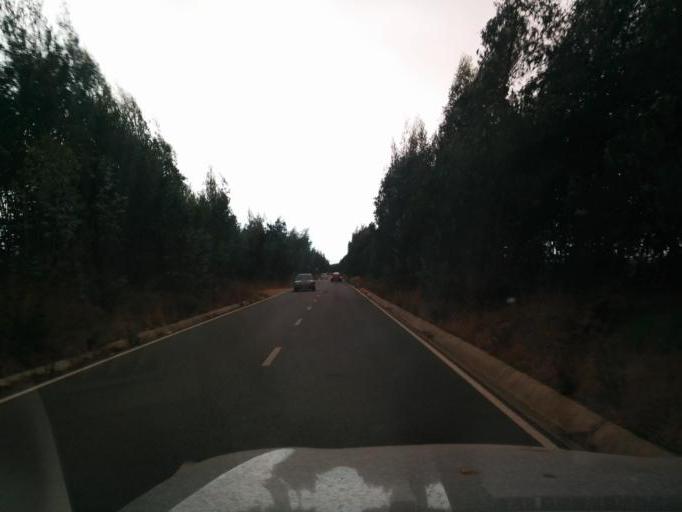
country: PT
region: Beja
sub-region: Odemira
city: Sao Teotonio
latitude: 37.5814
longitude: -8.7385
